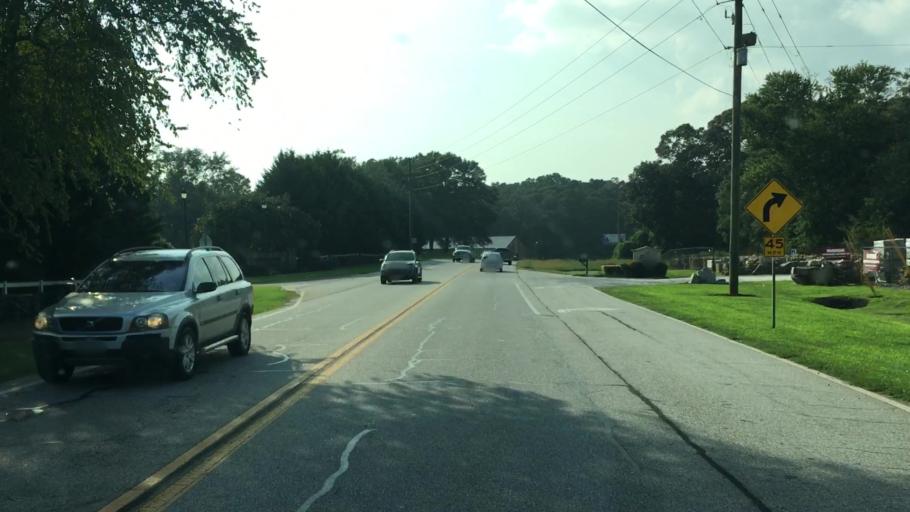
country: US
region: Georgia
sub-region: Jackson County
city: Braselton
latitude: 34.1376
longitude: -83.7909
